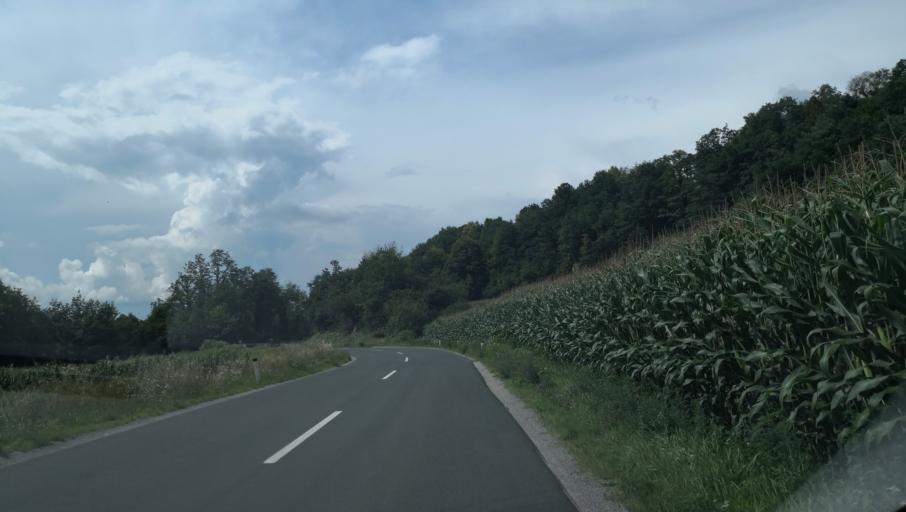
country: SI
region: Zuzemberk
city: Zuzemberk
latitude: 45.8138
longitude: 14.9638
